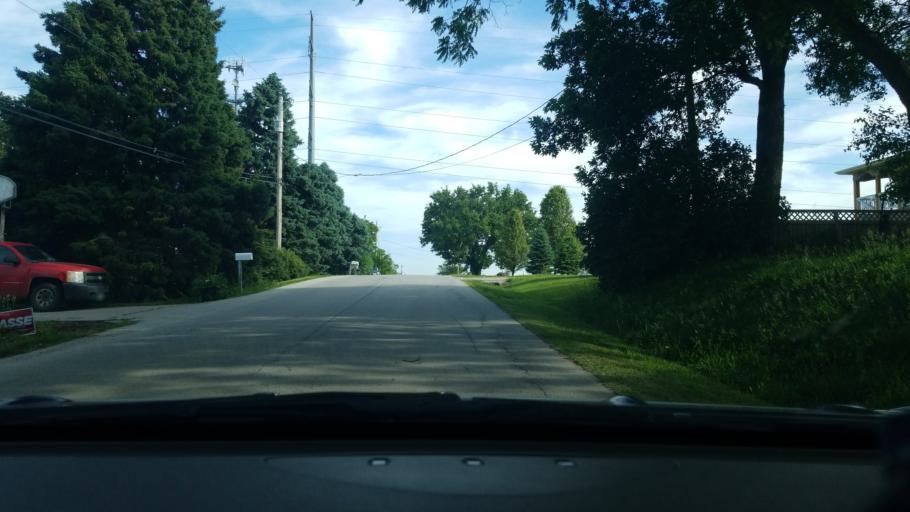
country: US
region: Nebraska
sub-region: Sarpy County
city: Offutt Air Force Base
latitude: 41.1700
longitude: -95.9335
